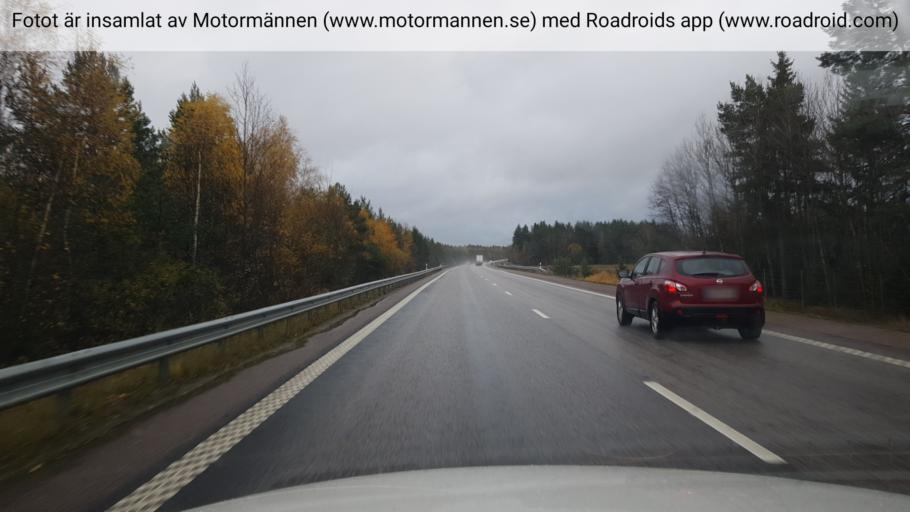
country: SE
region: Stockholm
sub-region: Sigtuna Kommun
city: Marsta
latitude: 59.6670
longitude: 17.8763
